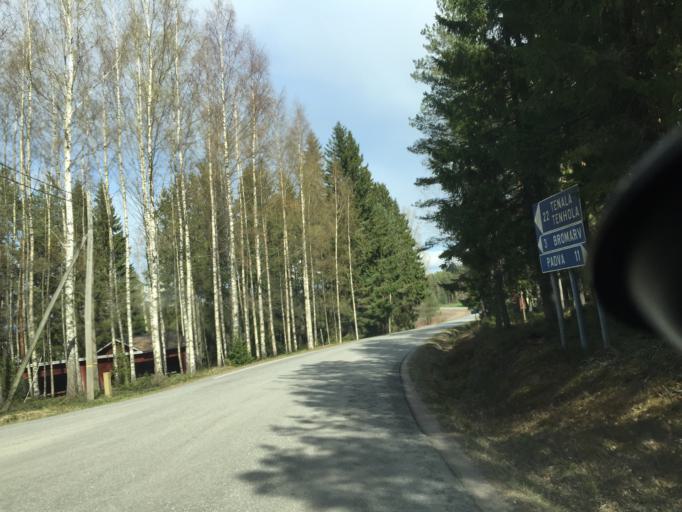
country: FI
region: Uusimaa
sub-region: Raaseporin
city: Hanko
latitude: 59.9691
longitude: 22.9802
